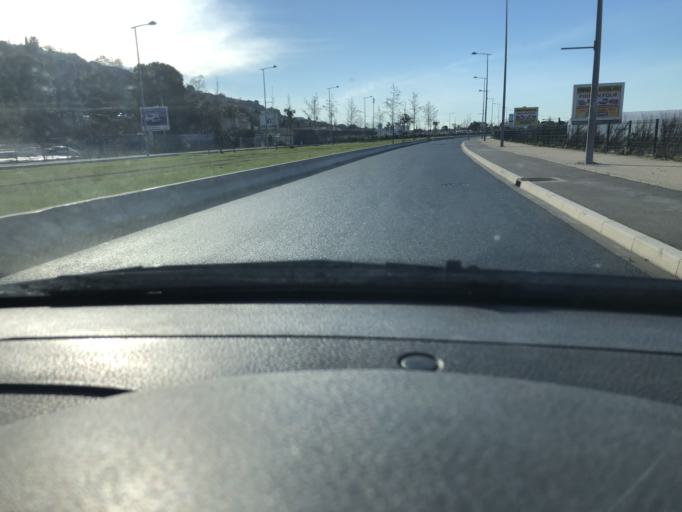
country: FR
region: Provence-Alpes-Cote d'Azur
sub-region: Departement des Alpes-Maritimes
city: Saint-Laurent-du-Var
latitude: 43.7040
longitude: 7.1968
